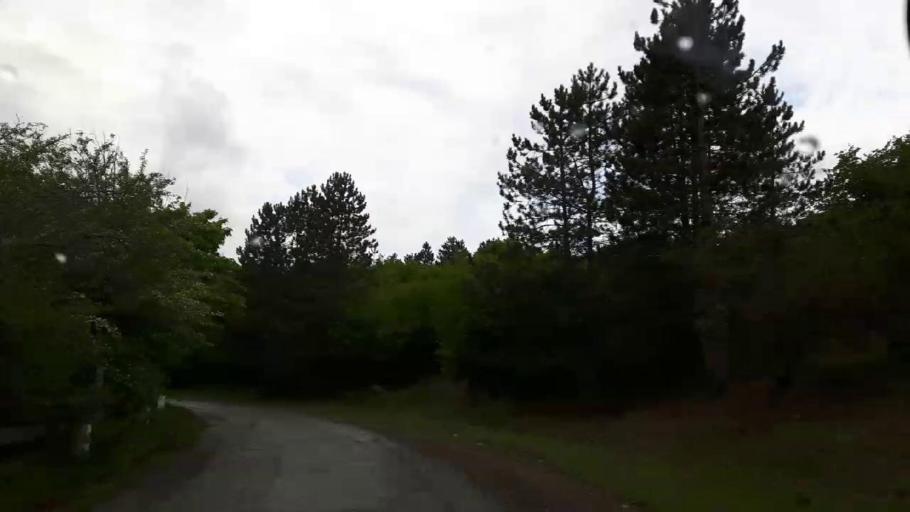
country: GE
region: Shida Kartli
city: Gori
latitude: 41.8951
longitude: 44.0389
